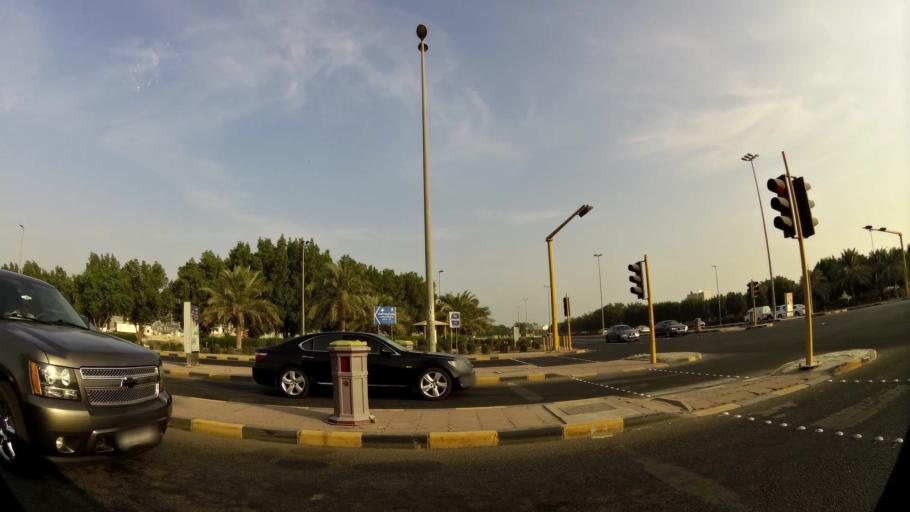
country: KW
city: Al Funaytis
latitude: 29.2261
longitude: 48.0815
